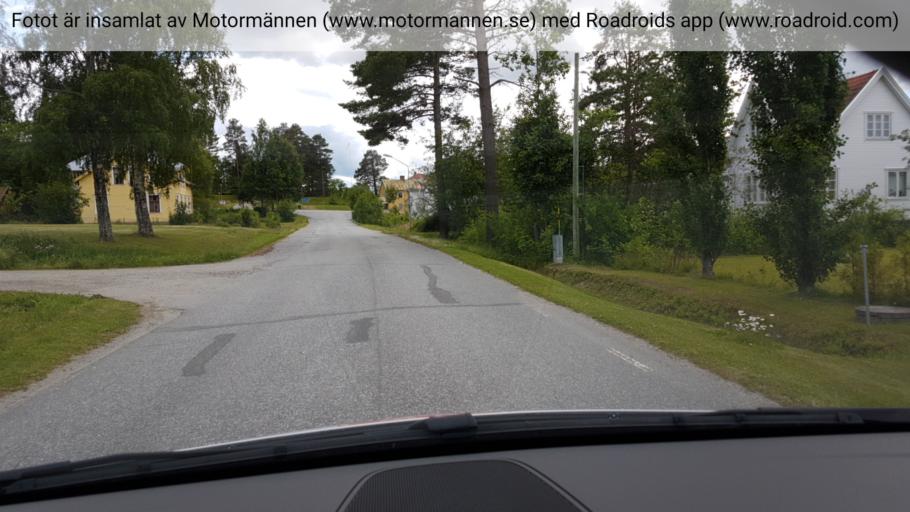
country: SE
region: Vaesterbotten
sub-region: Dorotea Kommun
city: Dorotea
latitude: 63.9225
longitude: 16.3417
